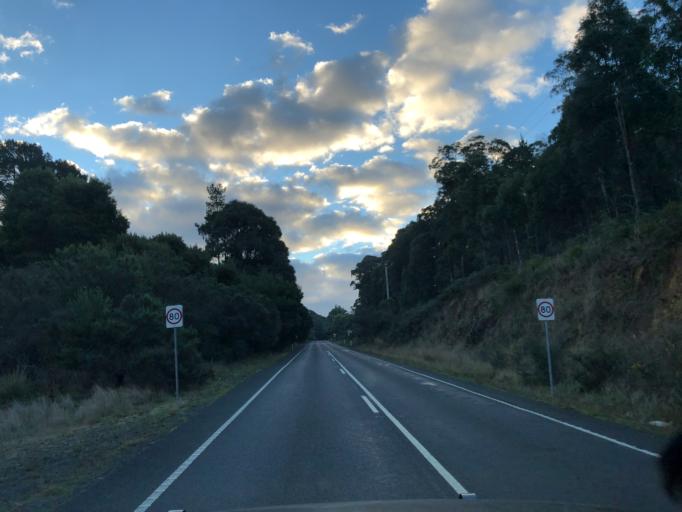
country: AU
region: Victoria
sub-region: Moorabool
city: Bacchus Marsh
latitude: -37.4533
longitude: 144.2950
